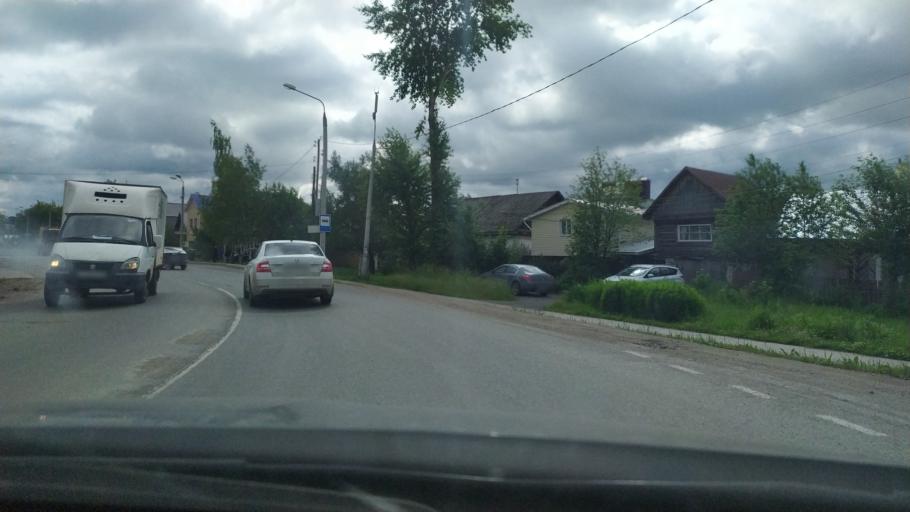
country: RU
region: Perm
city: Froly
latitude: 57.9771
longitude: 56.3058
